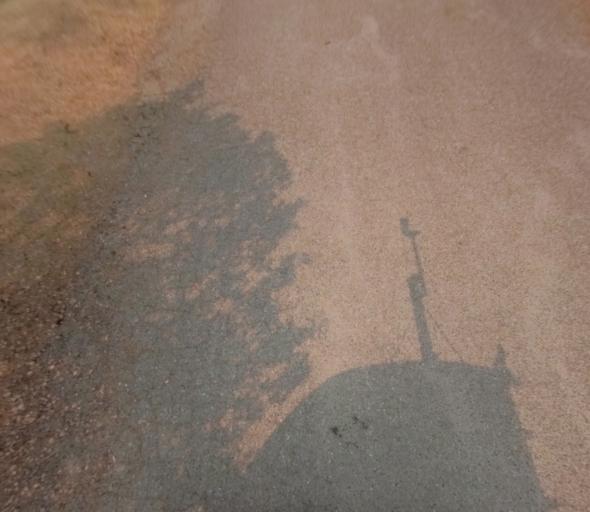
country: US
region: California
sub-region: Madera County
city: Oakhurst
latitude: 37.2974
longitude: -119.6024
